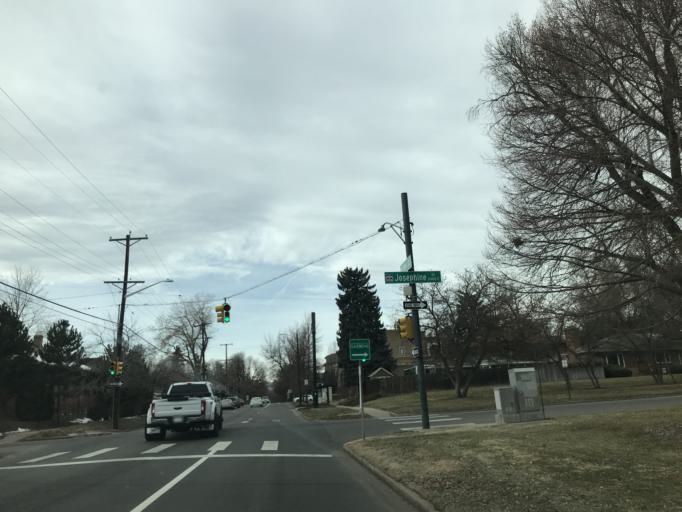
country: US
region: Colorado
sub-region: Denver County
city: Denver
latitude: 39.7292
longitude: -104.9587
